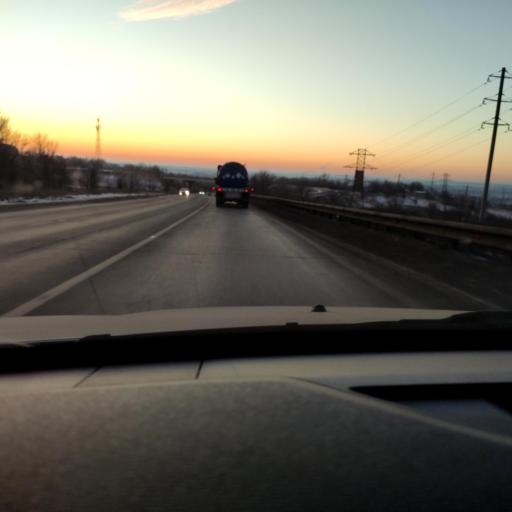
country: RU
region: Samara
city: Smyshlyayevka
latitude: 53.2437
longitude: 50.4776
